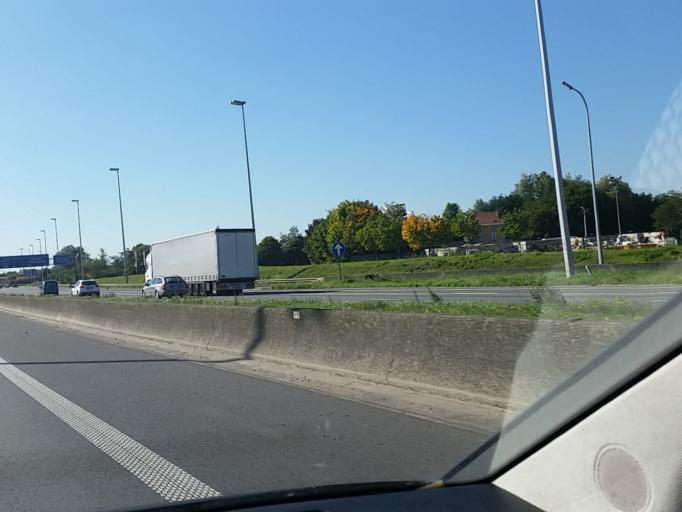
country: BE
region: Flanders
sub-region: Provincie Vlaams-Brabant
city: Wemmel
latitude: 50.8817
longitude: 4.2836
